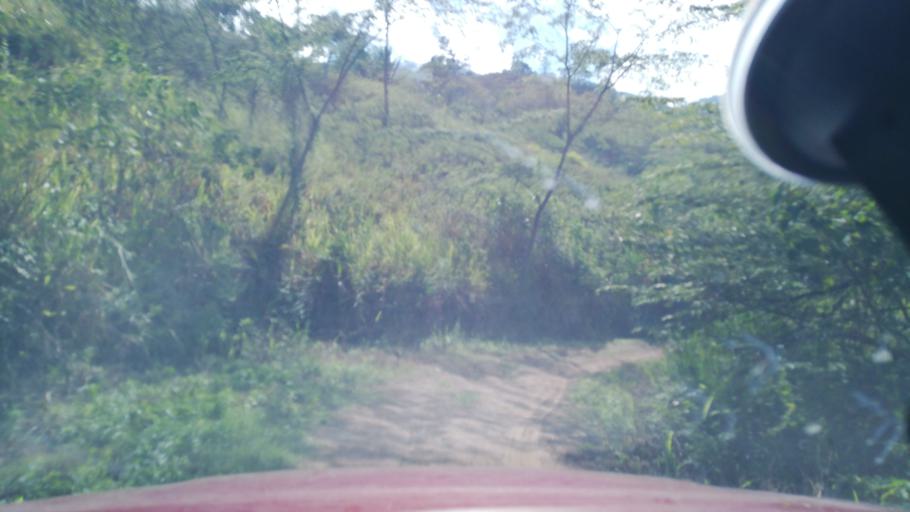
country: CO
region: Cundinamarca
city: Quipile
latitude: 4.7411
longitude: -74.6105
